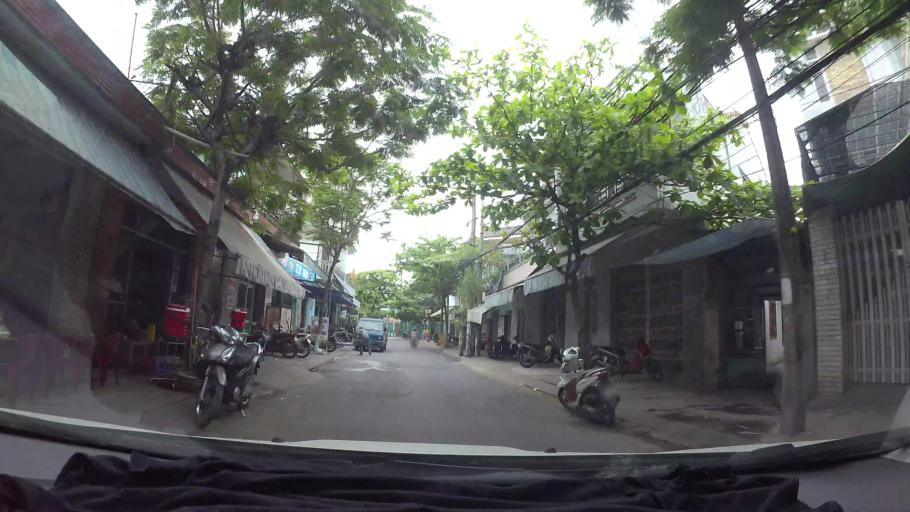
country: VN
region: Da Nang
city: Thanh Khe
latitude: 16.0667
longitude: 108.1806
